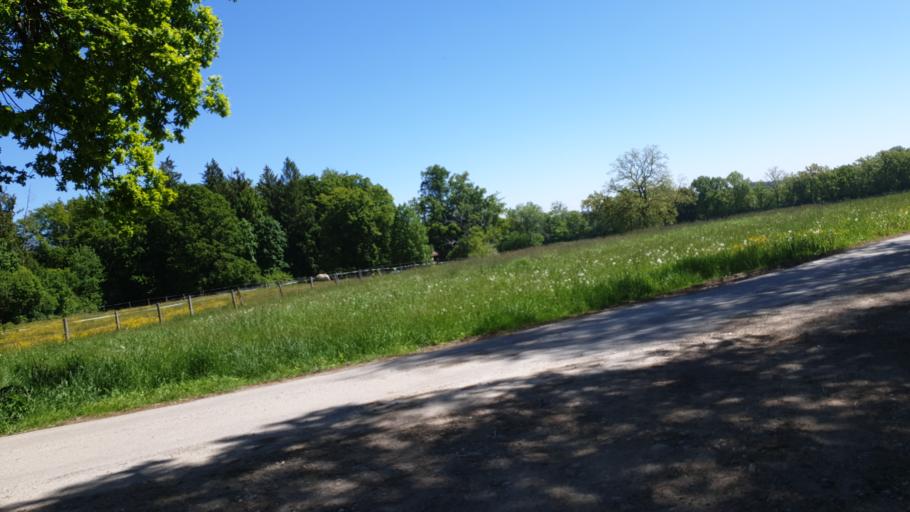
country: DE
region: Bavaria
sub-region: Upper Bavaria
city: Iffeldorf
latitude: 47.7684
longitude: 11.2979
